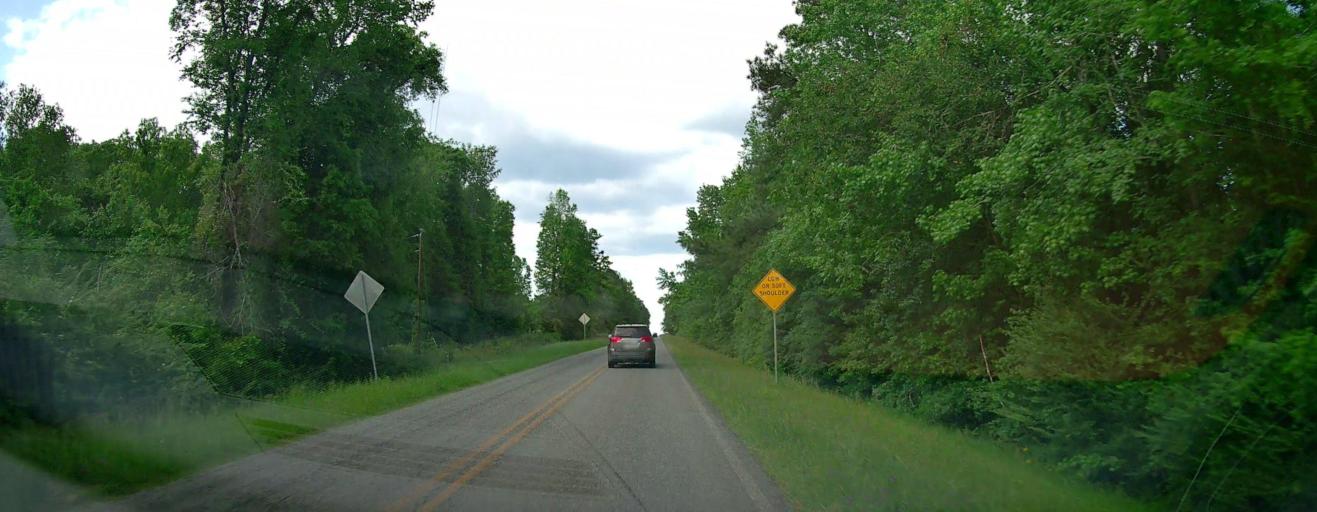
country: US
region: Georgia
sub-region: Laurens County
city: East Dublin
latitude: 32.6744
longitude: -82.8952
